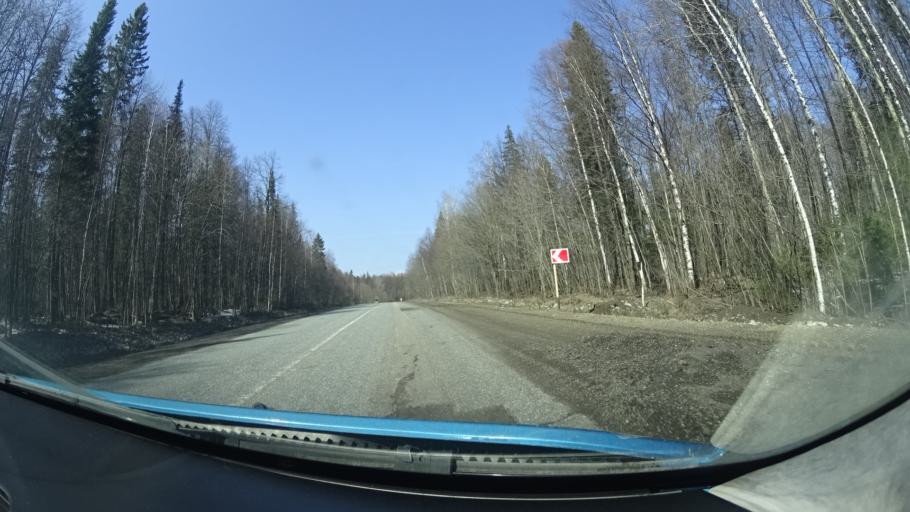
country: RU
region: Perm
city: Yugo-Kamskiy
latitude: 57.5057
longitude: 55.6874
